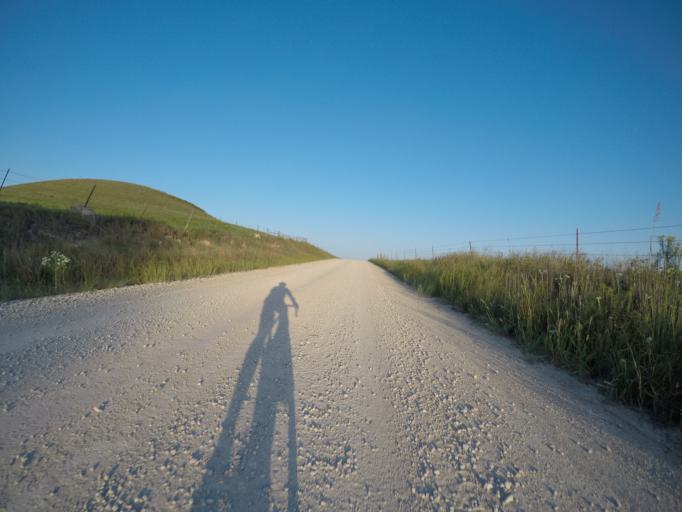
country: US
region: Kansas
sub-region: Riley County
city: Ogden
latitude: 39.0133
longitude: -96.6566
